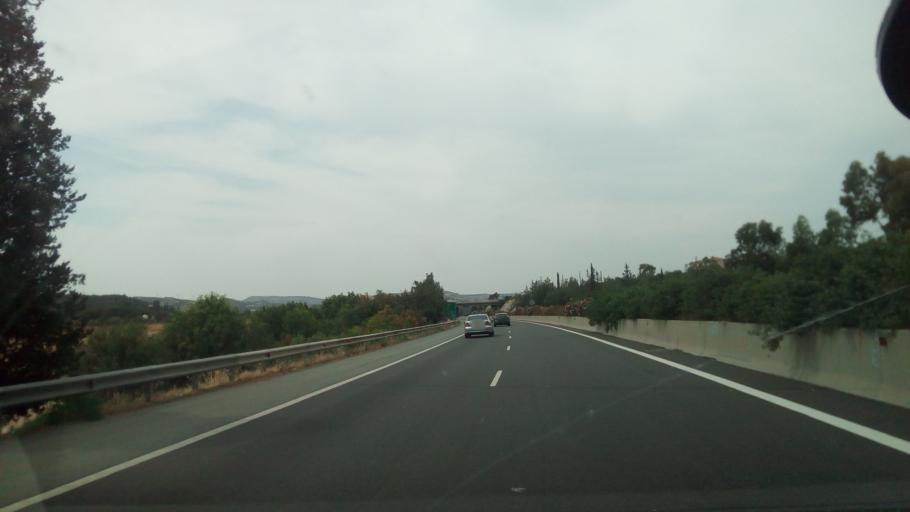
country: CY
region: Larnaka
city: Aradippou
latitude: 34.9616
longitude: 33.5680
